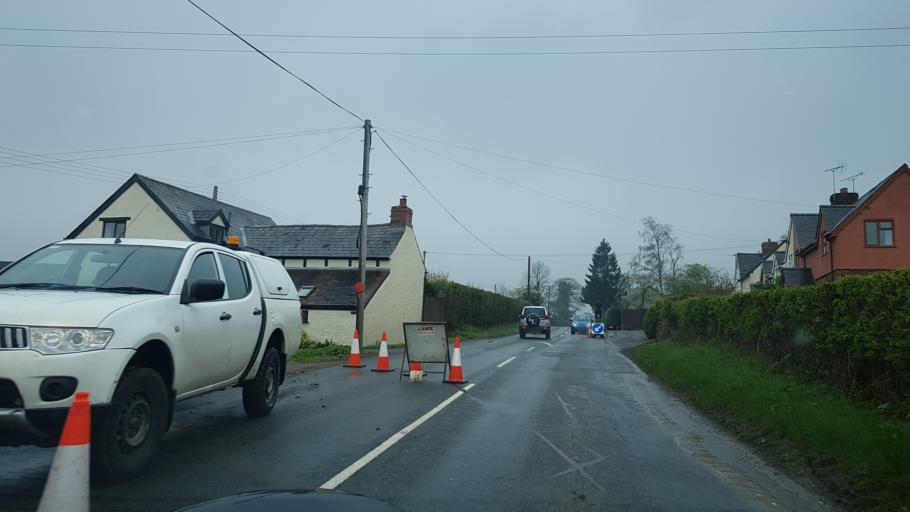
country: GB
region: England
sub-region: Herefordshire
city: Bromyard
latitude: 52.1612
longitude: -2.5359
